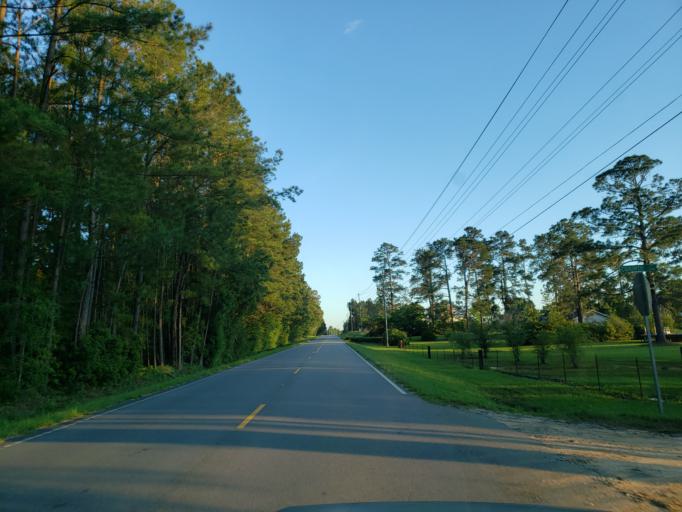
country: US
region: Georgia
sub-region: Lowndes County
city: Valdosta
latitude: 30.7084
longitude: -83.2418
